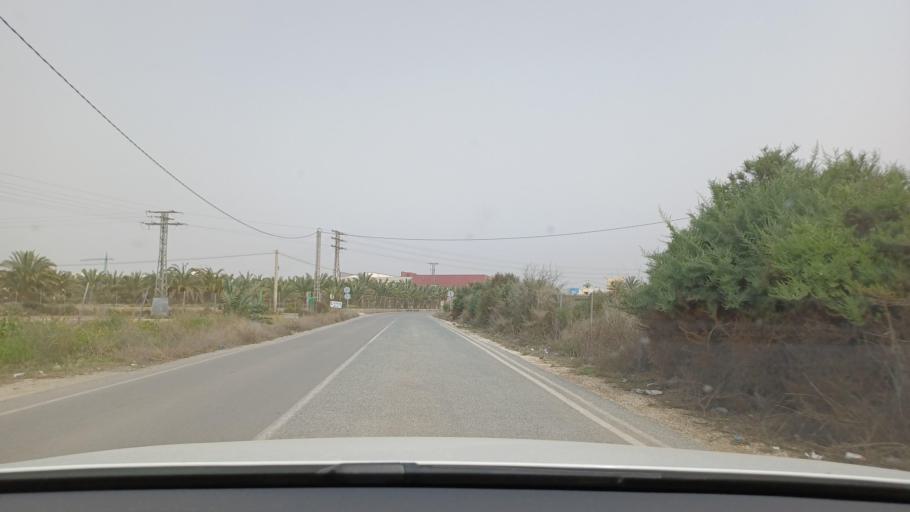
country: ES
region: Valencia
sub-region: Provincia de Alicante
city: Elche
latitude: 38.2480
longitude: -0.6912
